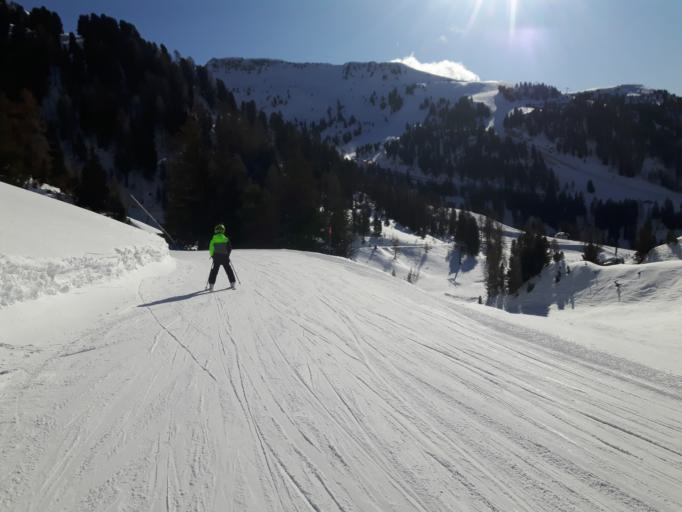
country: IT
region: Trentino-Alto Adige
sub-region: Provincia di Trento
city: Predazzo
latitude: 46.3465
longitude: 11.5530
